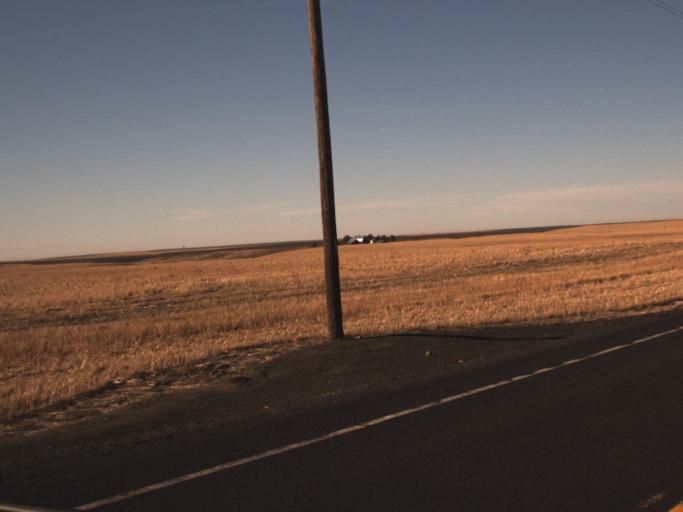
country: US
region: Washington
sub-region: Adams County
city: Ritzville
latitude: 46.9031
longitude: -118.3331
